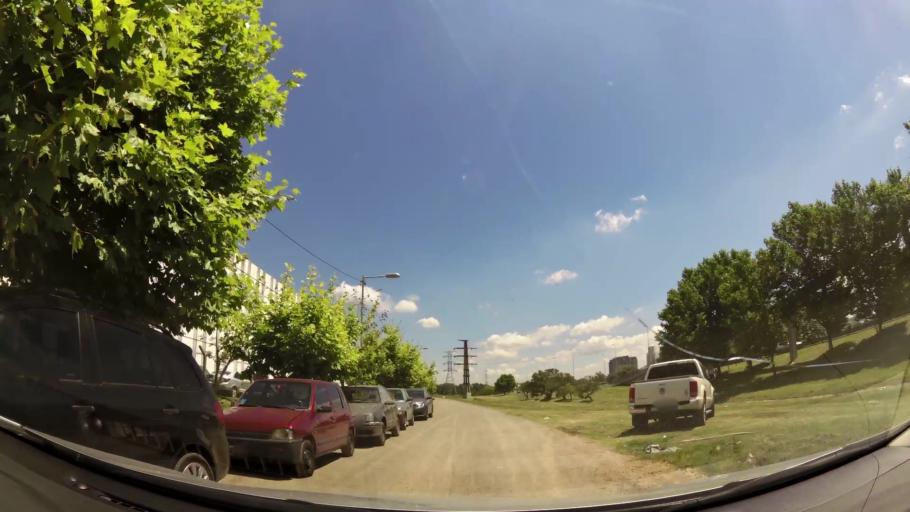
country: AR
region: Buenos Aires
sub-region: Partido de Tigre
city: Tigre
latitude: -34.4395
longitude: -58.5847
